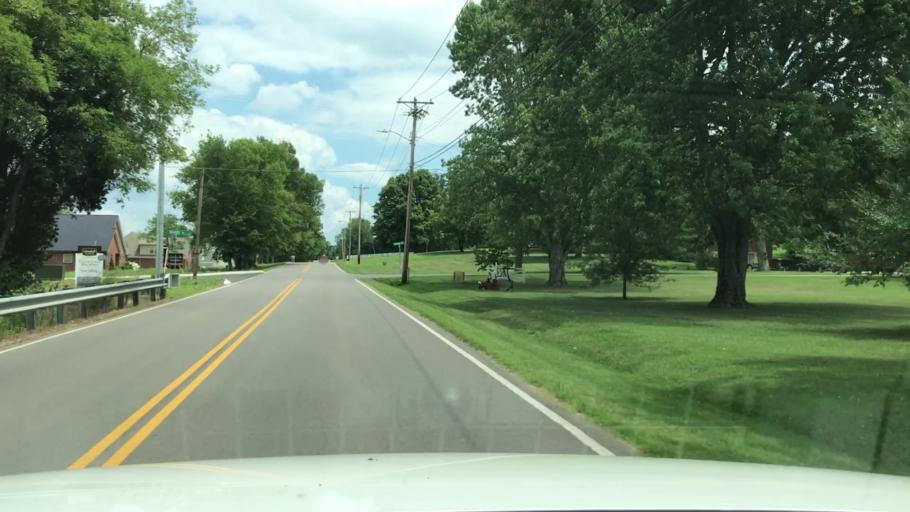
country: US
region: Tennessee
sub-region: Sumner County
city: Gallatin
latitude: 36.3601
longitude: -86.4556
